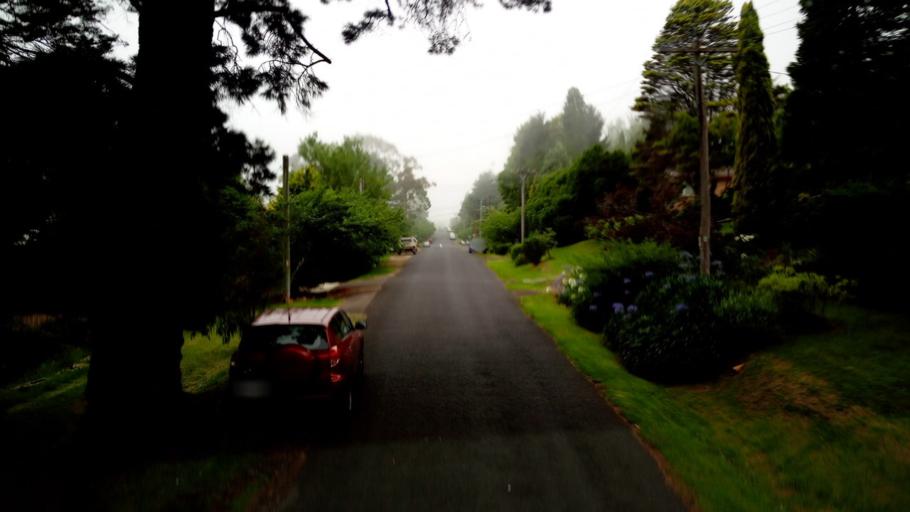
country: AU
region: New South Wales
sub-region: Blue Mountains Municipality
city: Leura
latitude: -33.7163
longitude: 150.3368
